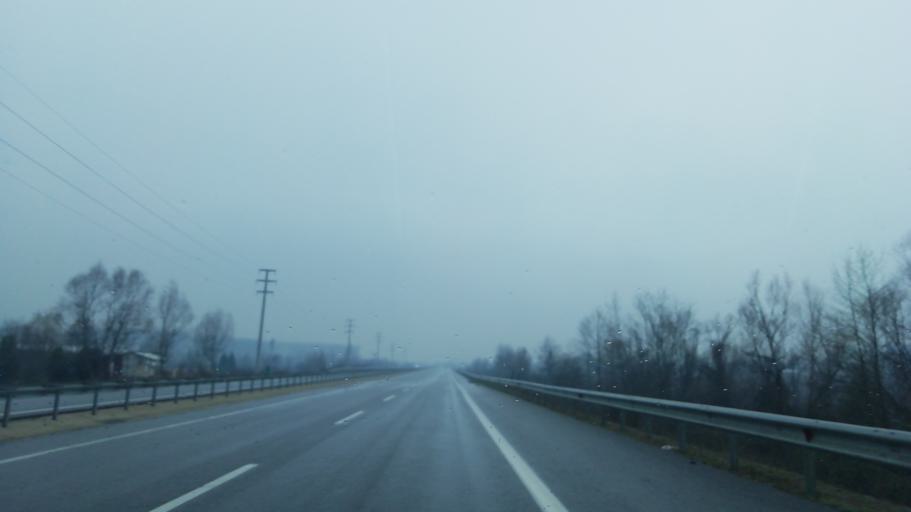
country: TR
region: Sakarya
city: Akyazi
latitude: 40.6540
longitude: 30.6001
